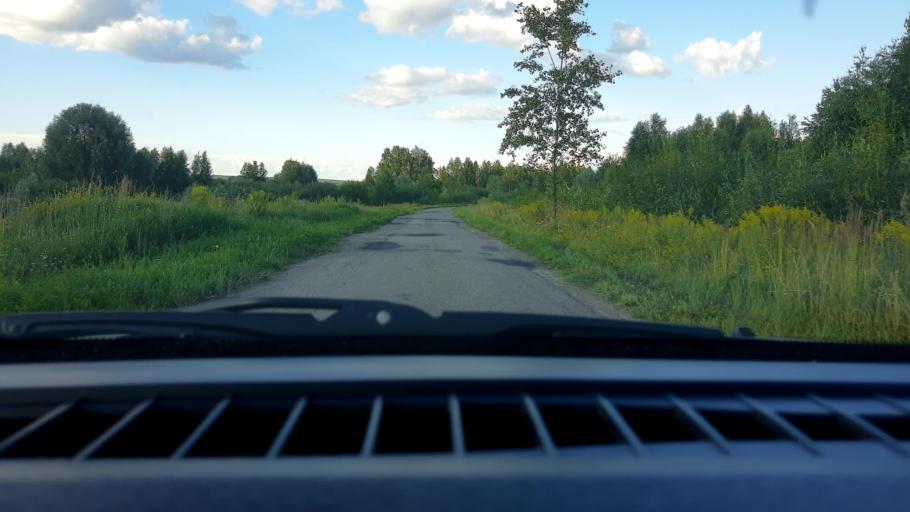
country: RU
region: Nizjnij Novgorod
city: Afonino
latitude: 56.1295
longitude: 44.0586
